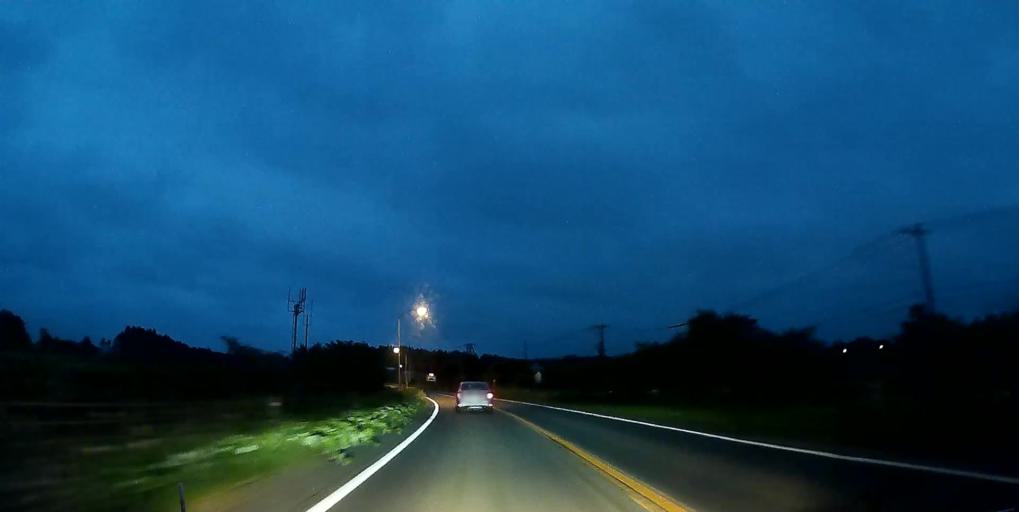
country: JP
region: Hokkaido
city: Nanae
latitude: 42.2094
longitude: 140.3961
